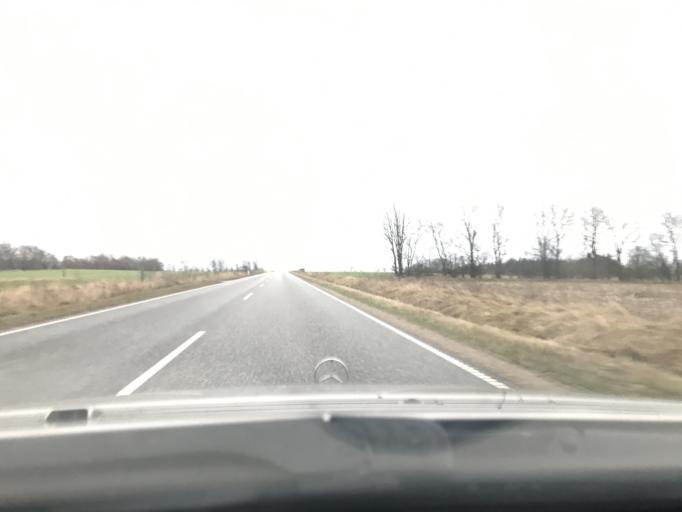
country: DK
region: South Denmark
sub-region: Tonder Kommune
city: Toftlund
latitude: 55.1167
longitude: 9.1626
